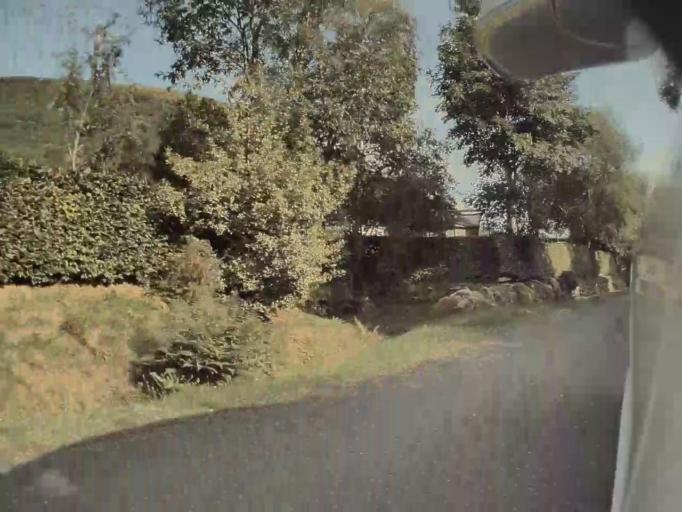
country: IE
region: Leinster
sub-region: Wicklow
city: Rathdrum
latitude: 53.0513
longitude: -6.3303
